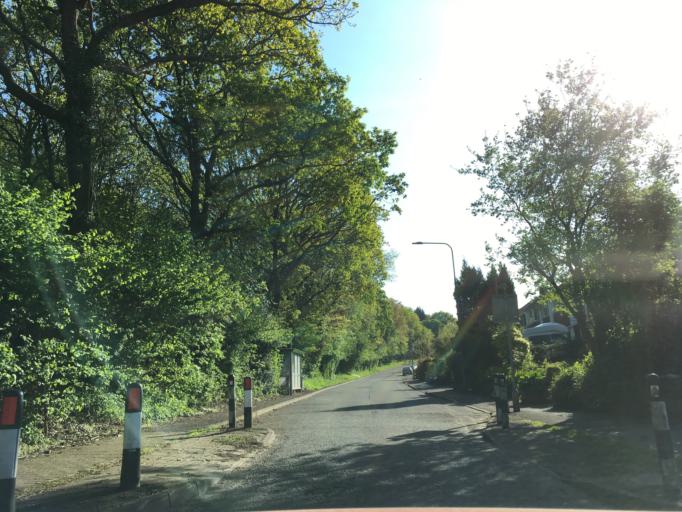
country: GB
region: Wales
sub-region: Cardiff
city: Cardiff
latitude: 51.5310
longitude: -3.1602
